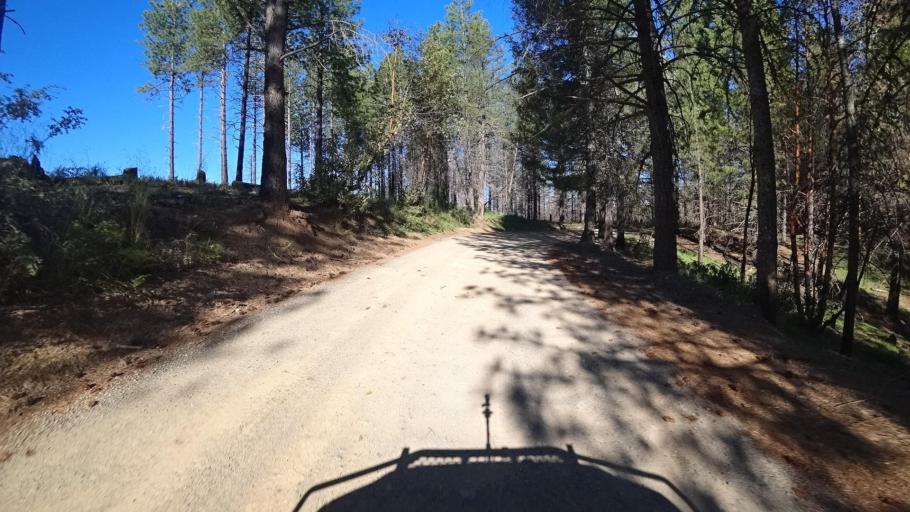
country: US
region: California
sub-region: Lake County
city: Upper Lake
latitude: 39.3497
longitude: -122.9733
